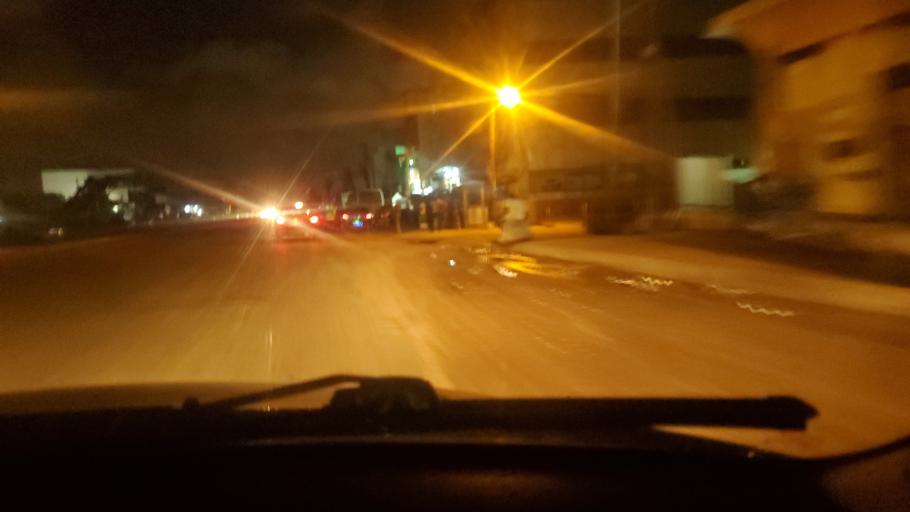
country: SN
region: Dakar
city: Pikine
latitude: 14.7441
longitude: -17.3852
